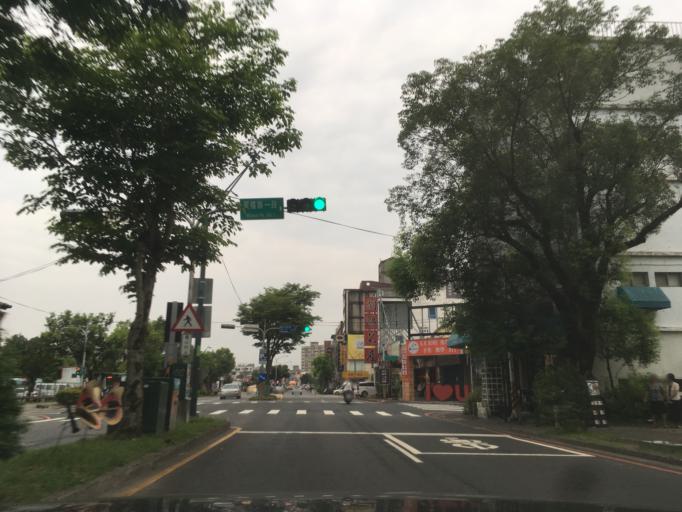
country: TW
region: Taiwan
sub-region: Yilan
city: Yilan
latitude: 24.7526
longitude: 121.7565
